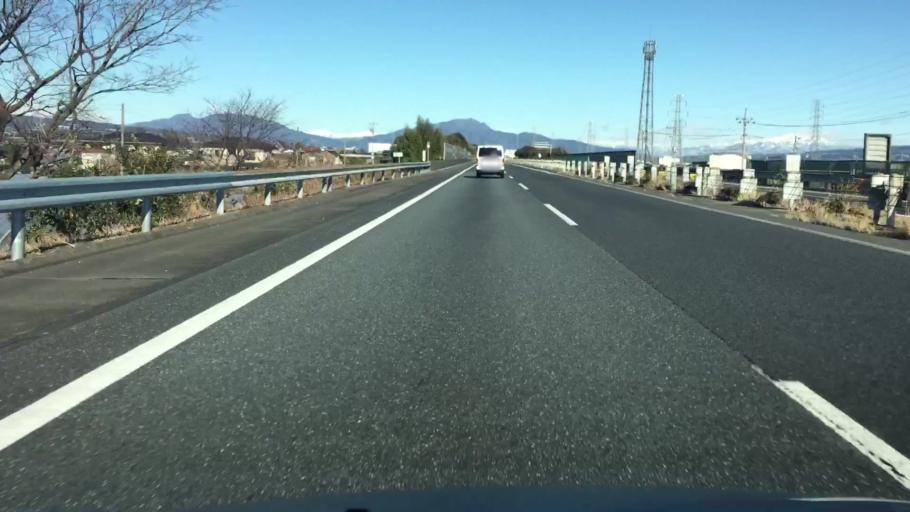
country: JP
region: Gunma
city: Kanekomachi
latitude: 36.3934
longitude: 139.0254
